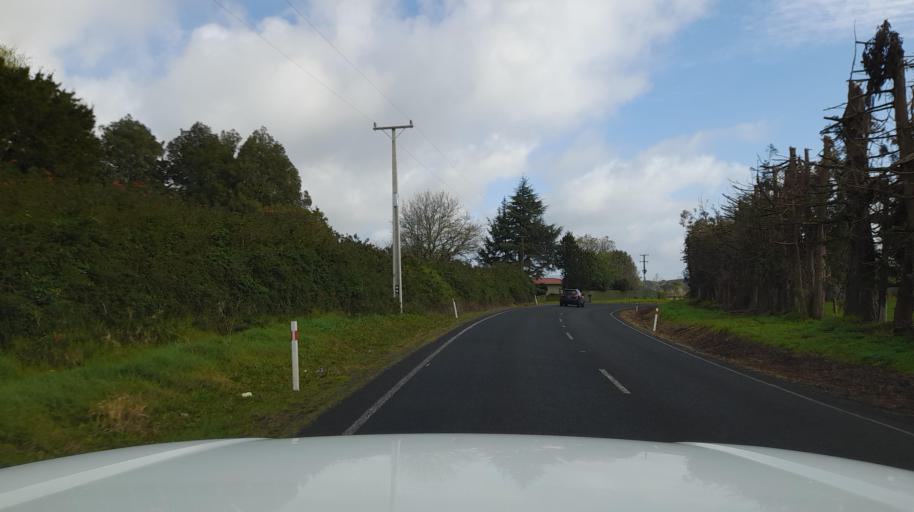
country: NZ
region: Northland
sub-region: Far North District
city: Waimate North
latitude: -35.3523
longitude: 173.8265
